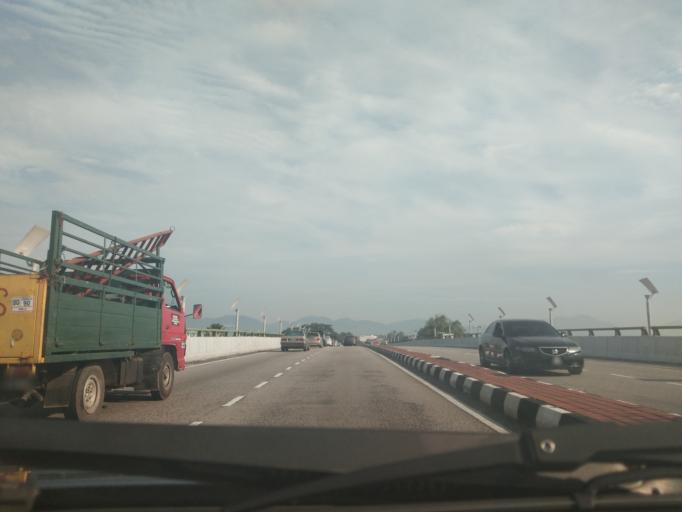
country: MY
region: Perak
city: Ipoh
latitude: 4.5782
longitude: 101.1061
